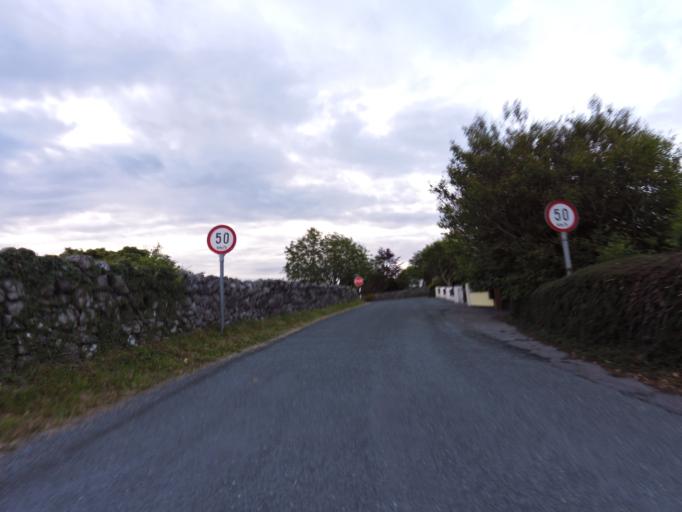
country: IE
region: Connaught
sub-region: County Galway
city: Athenry
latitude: 53.2984
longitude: -8.7374
